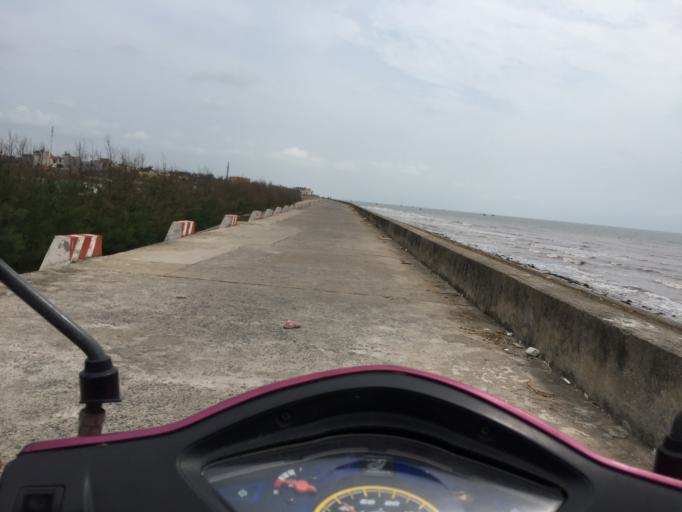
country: VN
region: Ninh Binh
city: Thi Tran Phat Diem
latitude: 20.0181
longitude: 106.2132
